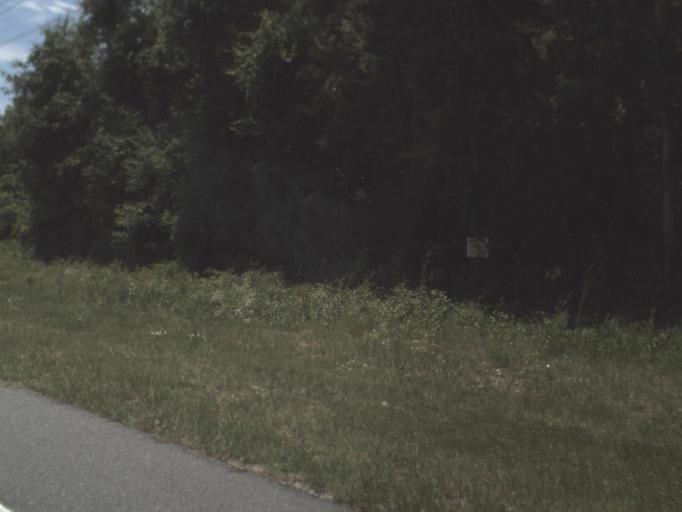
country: US
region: Florida
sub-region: Dixie County
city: Cross City
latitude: 29.7477
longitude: -82.9845
